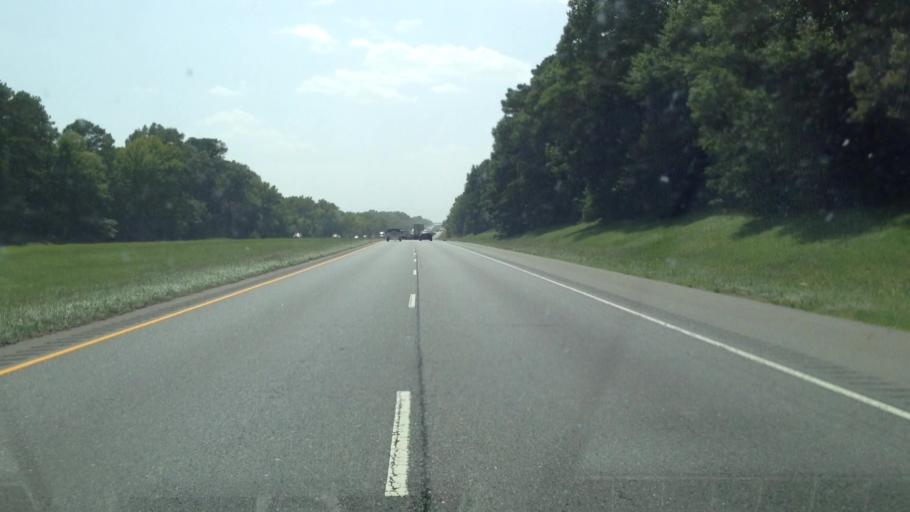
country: US
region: Louisiana
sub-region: Bossier Parish
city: Eastwood
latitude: 32.5423
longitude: -93.5707
